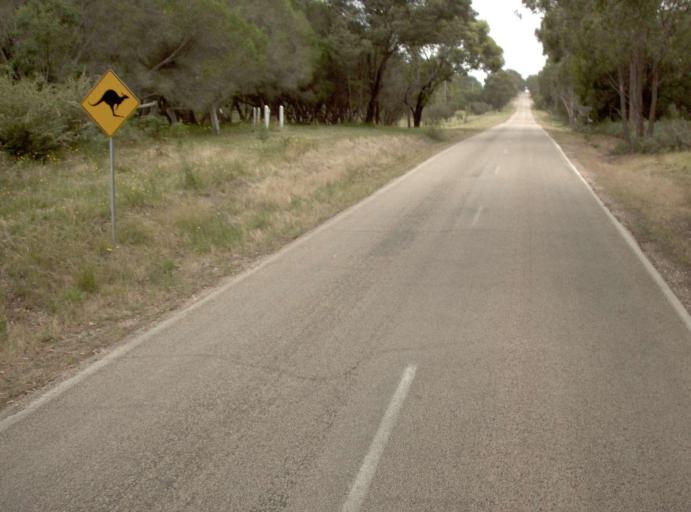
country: AU
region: Victoria
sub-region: East Gippsland
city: Bairnsdale
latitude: -37.8334
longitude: 147.4328
